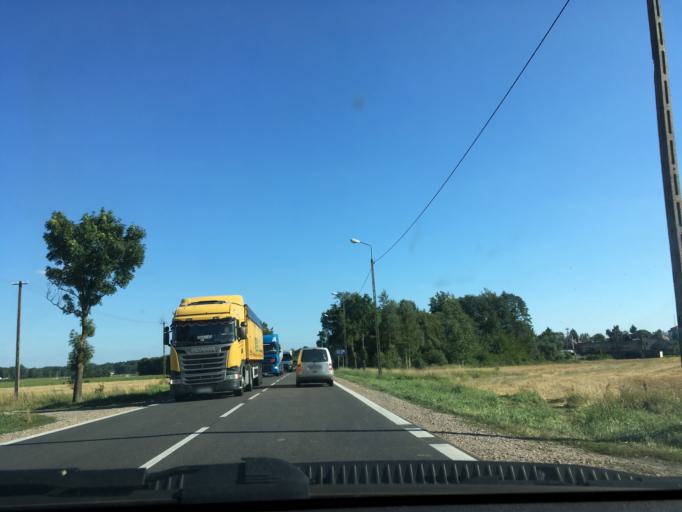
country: PL
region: Podlasie
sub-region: Powiat sokolski
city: Suchowola
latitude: 53.4487
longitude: 23.0902
